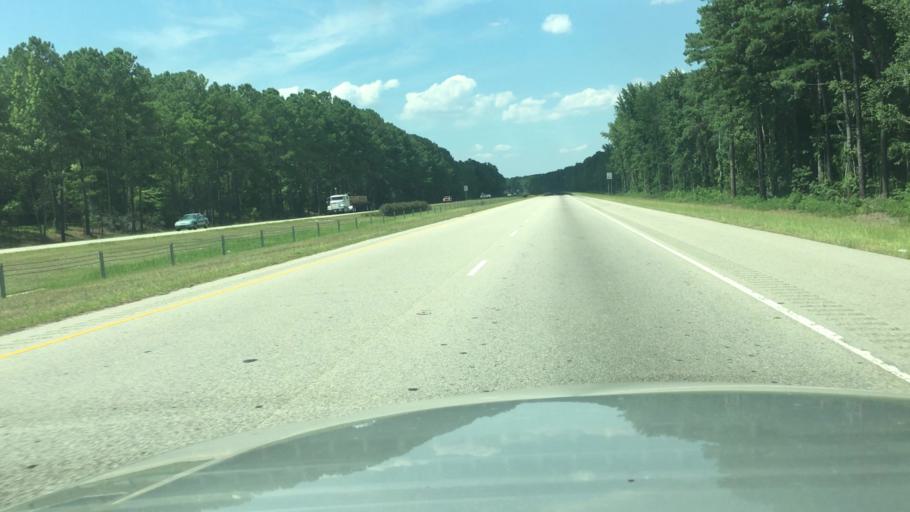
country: US
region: North Carolina
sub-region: Cumberland County
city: Fayetteville
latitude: 34.9871
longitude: -78.8609
